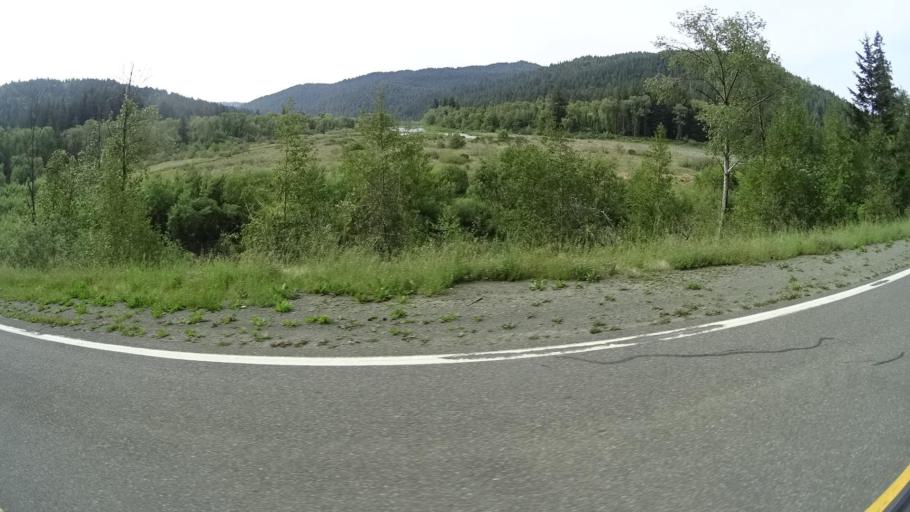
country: US
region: California
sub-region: Humboldt County
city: Redway
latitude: 40.2229
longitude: -123.7894
